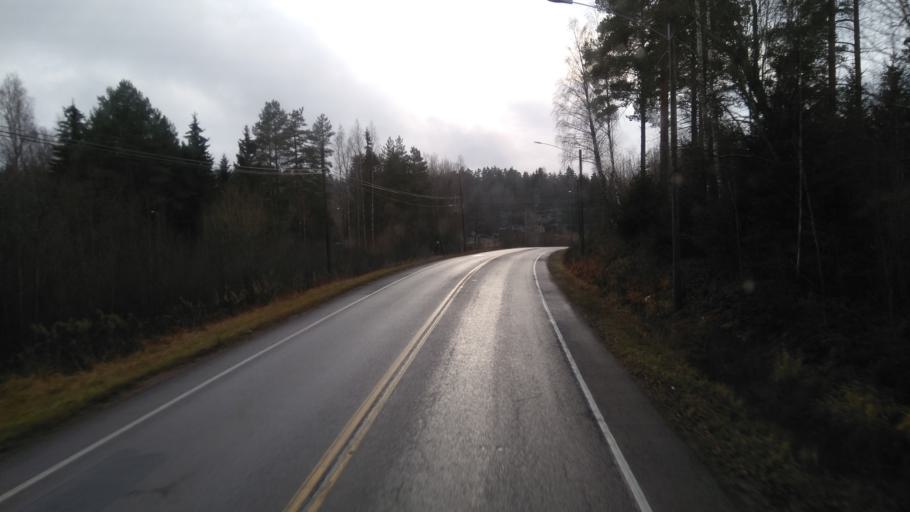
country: FI
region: Uusimaa
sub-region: Porvoo
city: Porvoo
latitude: 60.4155
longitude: 25.7035
